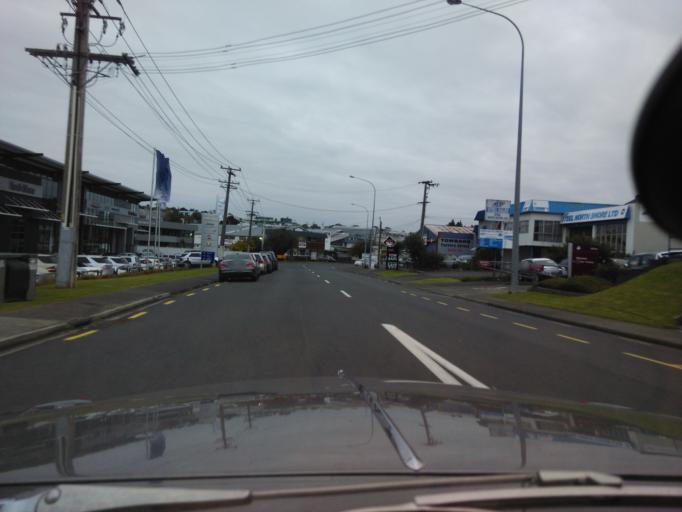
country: NZ
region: Auckland
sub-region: Auckland
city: North Shore
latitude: -36.7720
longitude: 174.7382
